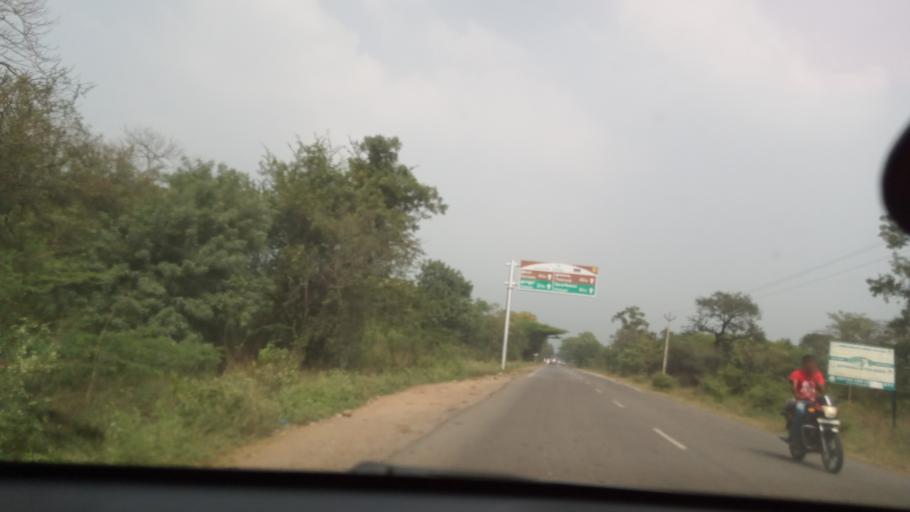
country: IN
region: Tamil Nadu
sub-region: Erode
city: Sathyamangalam
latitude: 11.5561
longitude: 77.1374
